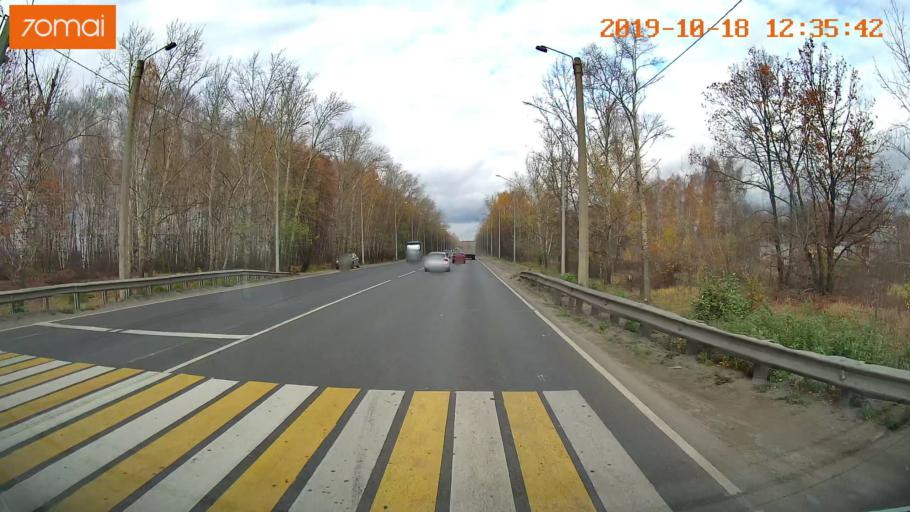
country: RU
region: Rjazan
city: Ryazan'
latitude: 54.6272
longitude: 39.6352
